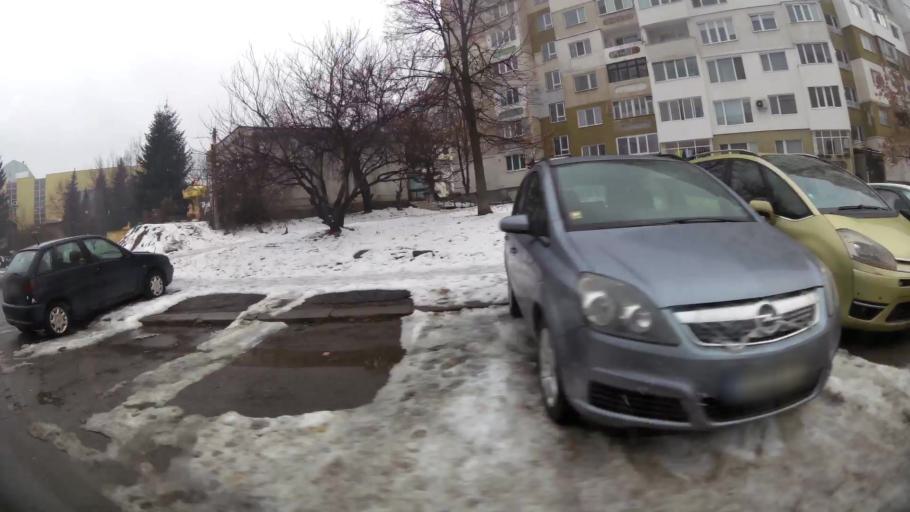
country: BG
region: Sofiya
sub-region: Obshtina Bozhurishte
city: Bozhurishte
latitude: 42.6874
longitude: 23.2462
